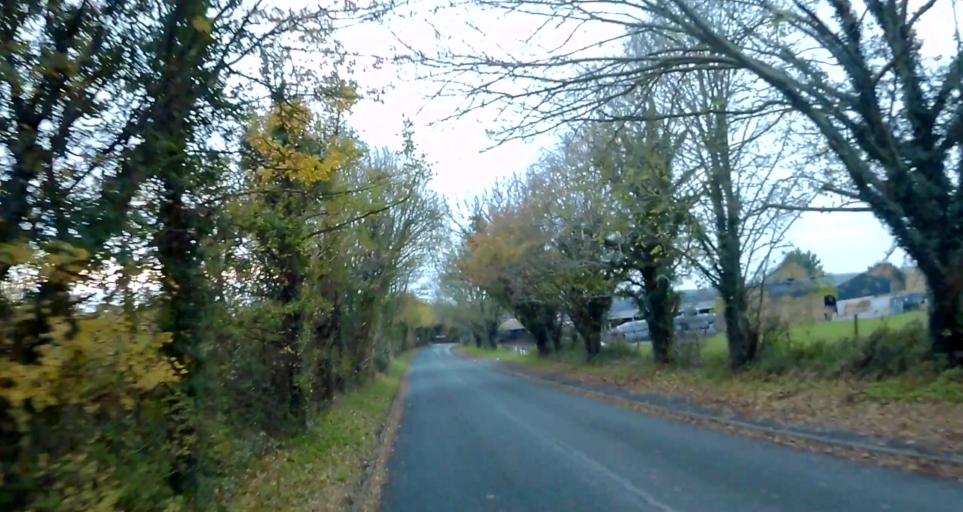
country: GB
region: England
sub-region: Hampshire
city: Odiham
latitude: 51.2533
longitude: -0.9563
